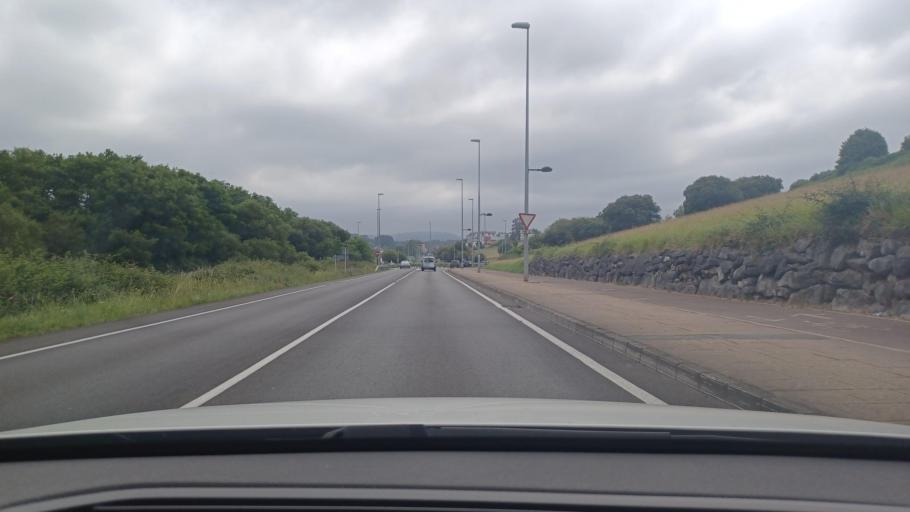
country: ES
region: Asturias
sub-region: Province of Asturias
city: Castrillon
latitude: 43.5675
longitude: -5.9644
